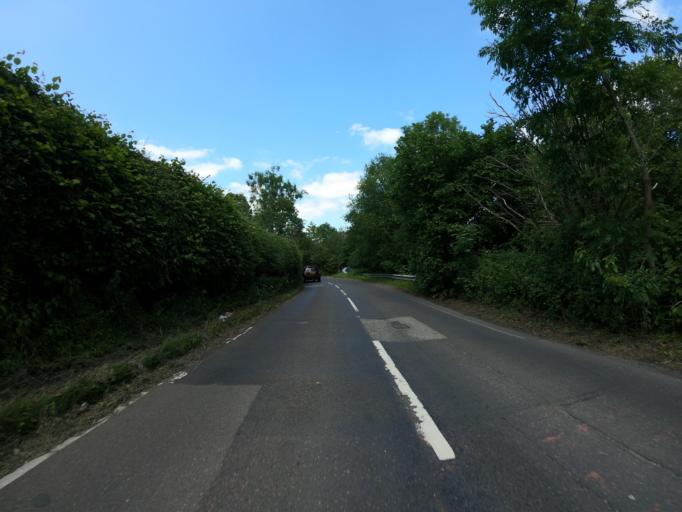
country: GB
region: England
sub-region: Kent
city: Halstead
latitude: 51.3147
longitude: 0.1346
